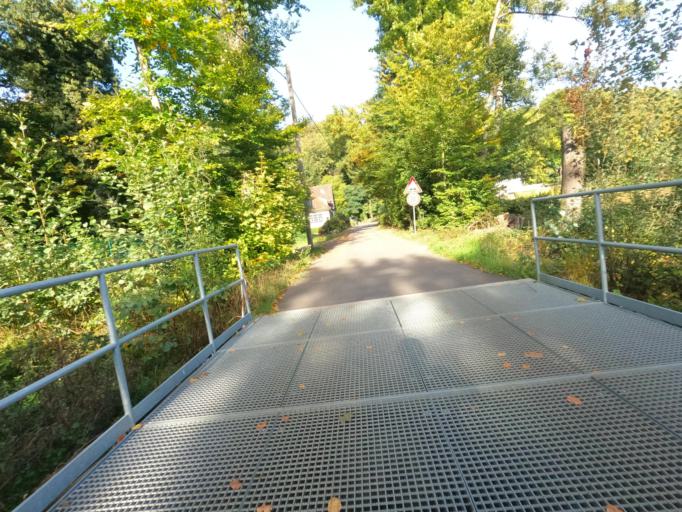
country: DE
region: North Rhine-Westphalia
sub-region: Regierungsbezirk Dusseldorf
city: Niederkruchten
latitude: 51.1476
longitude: 6.1926
